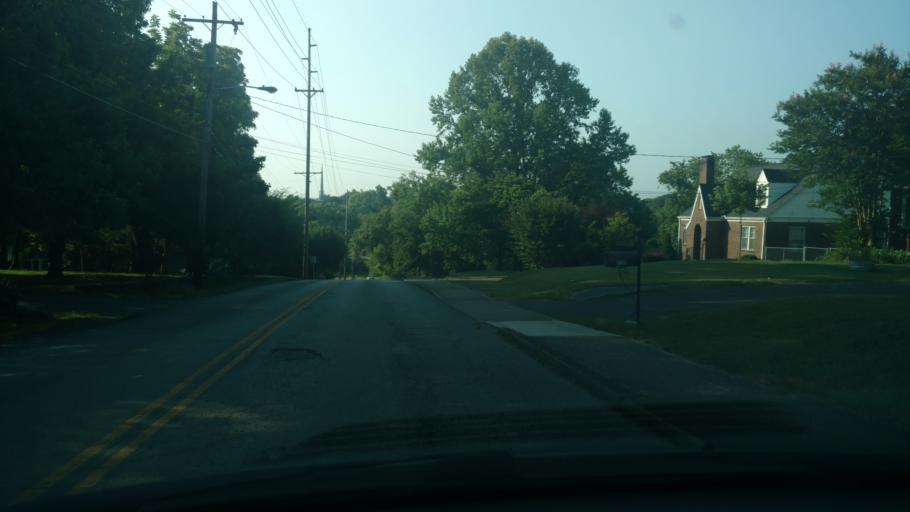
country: US
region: Tennessee
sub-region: Davidson County
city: Nashville
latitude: 36.2094
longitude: -86.7182
